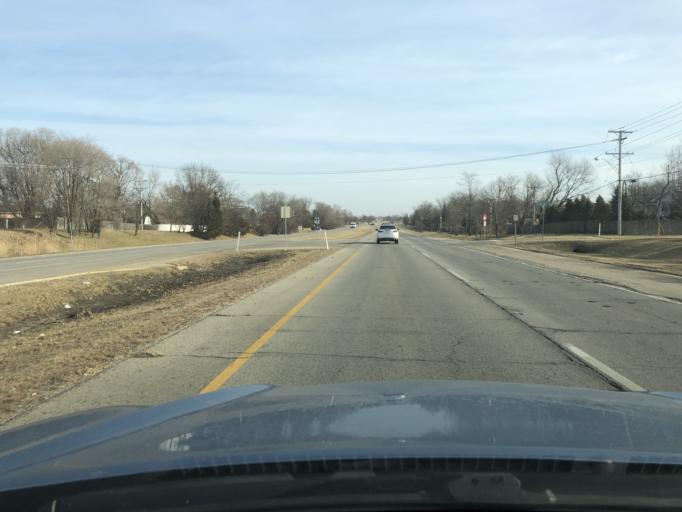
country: US
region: Illinois
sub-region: Cook County
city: South Barrington
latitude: 42.0536
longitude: -88.1199
